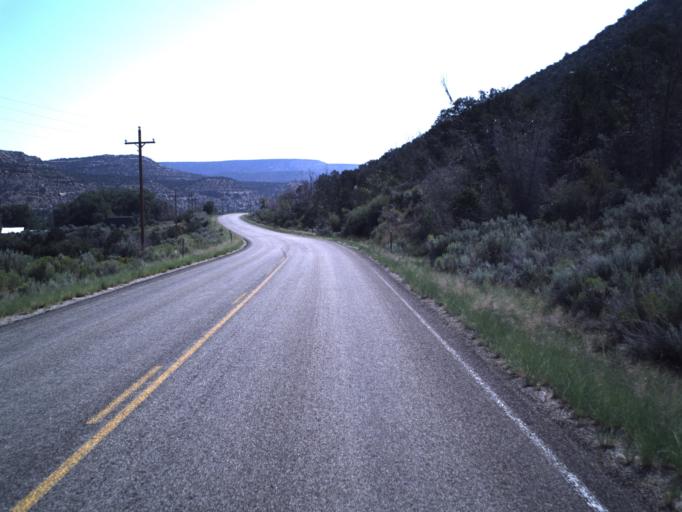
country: US
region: Utah
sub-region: Duchesne County
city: Duchesne
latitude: 40.2967
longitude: -110.5448
